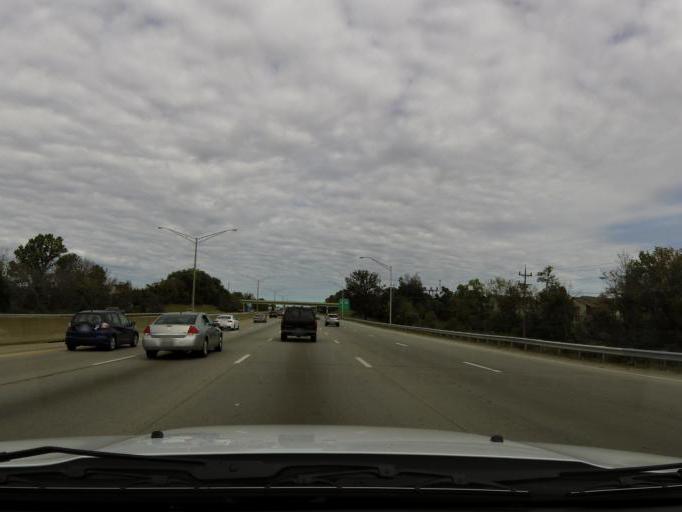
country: US
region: Kentucky
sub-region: Boone County
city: Florence
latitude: 38.9629
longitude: -84.6354
